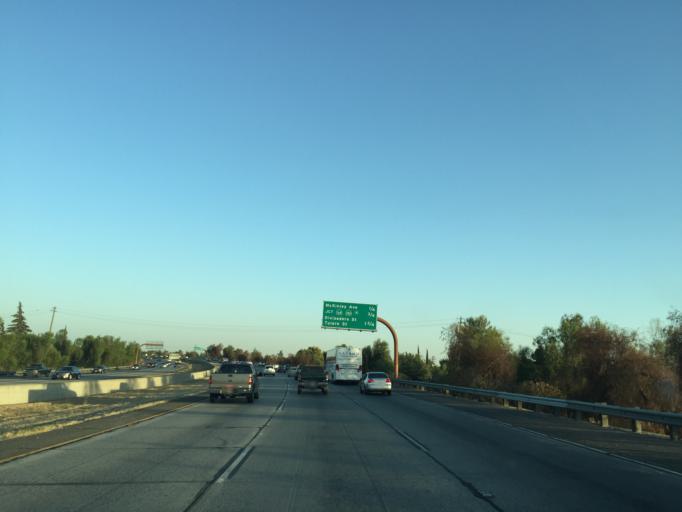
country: US
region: California
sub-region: Fresno County
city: Fresno
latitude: 36.7711
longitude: -119.7845
